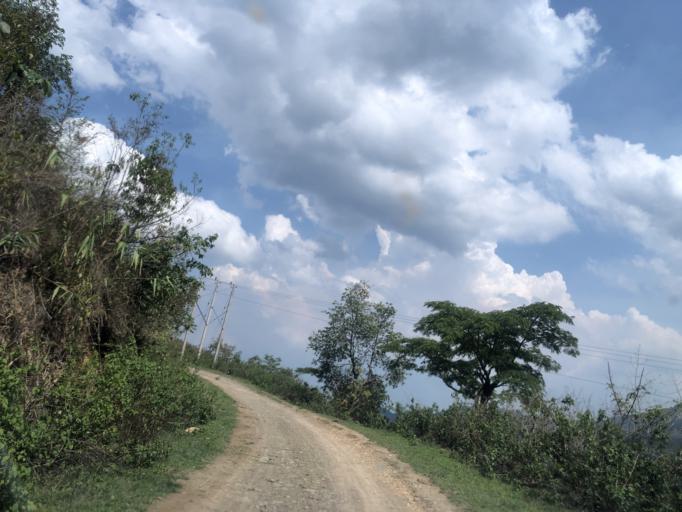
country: LA
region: Phongsali
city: Phongsali
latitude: 21.4082
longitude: 102.2359
